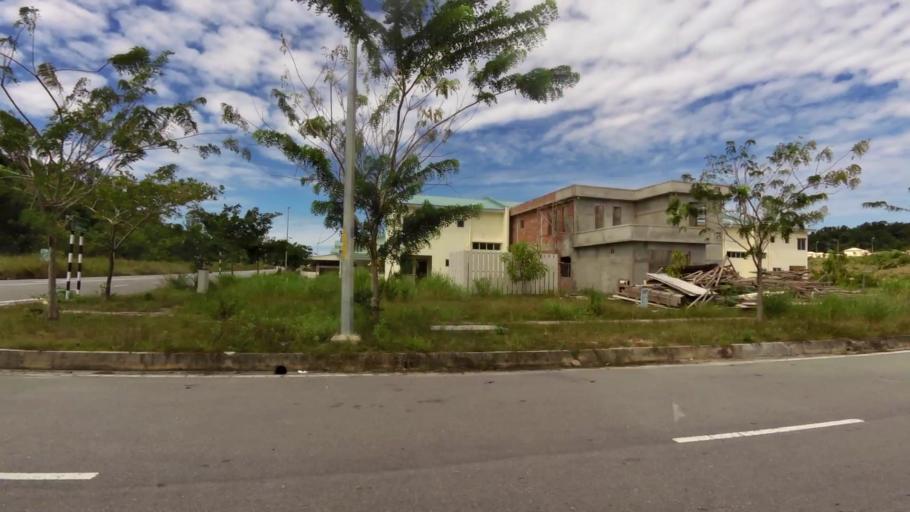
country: BN
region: Brunei and Muara
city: Bandar Seri Begawan
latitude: 4.9842
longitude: 115.0154
